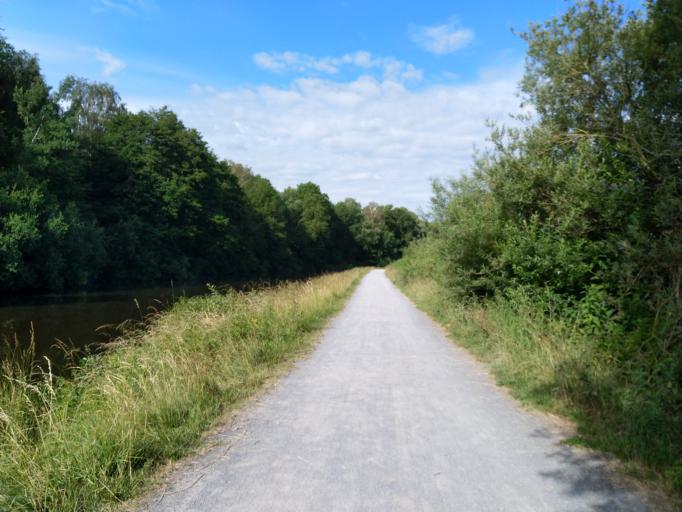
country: FR
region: Nord-Pas-de-Calais
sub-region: Departement du Nord
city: Marpent
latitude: 50.2861
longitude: 4.0653
